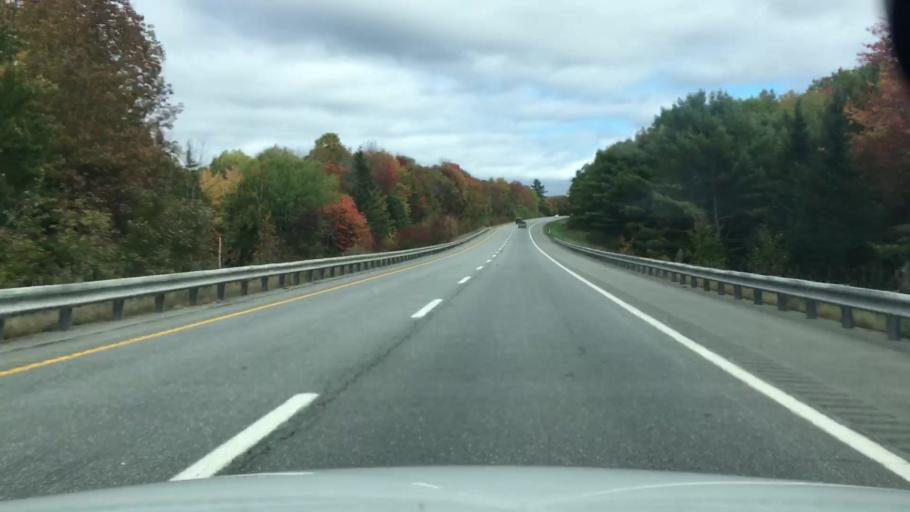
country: US
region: Maine
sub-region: Penobscot County
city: Carmel
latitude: 44.7732
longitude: -69.0171
